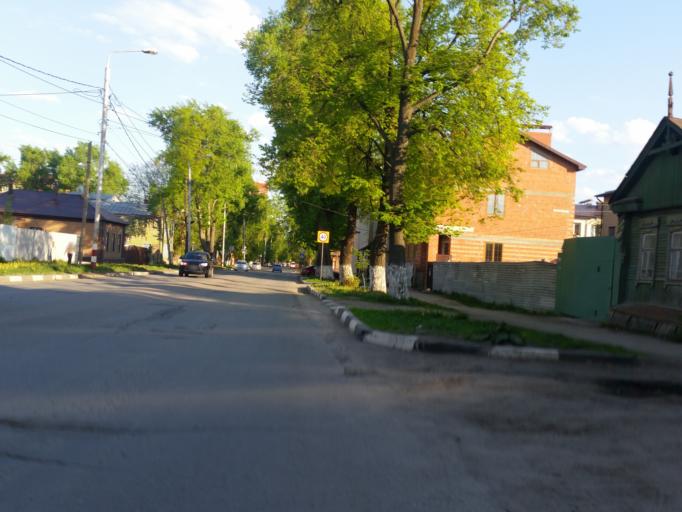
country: RU
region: Ulyanovsk
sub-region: Ulyanovskiy Rayon
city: Ulyanovsk
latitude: 54.3257
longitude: 48.3995
